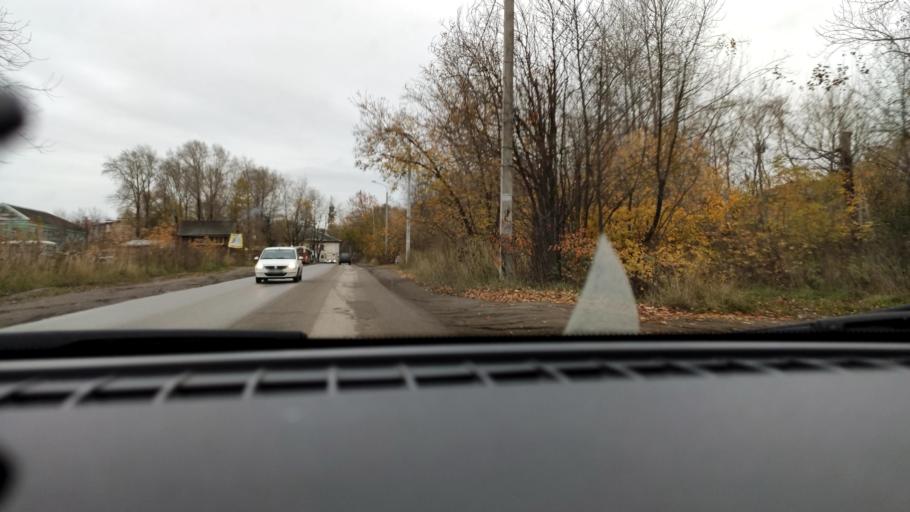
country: RU
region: Perm
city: Perm
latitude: 57.9762
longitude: 56.2805
